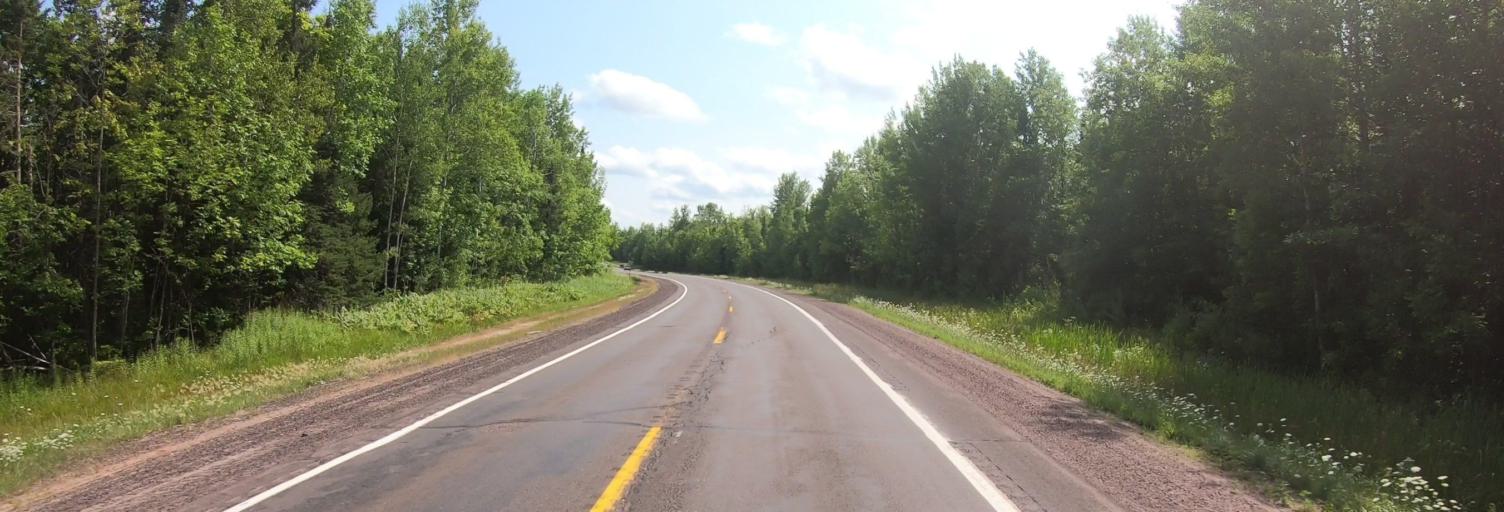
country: US
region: Michigan
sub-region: Ontonagon County
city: Ontonagon
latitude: 46.8284
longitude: -88.9970
